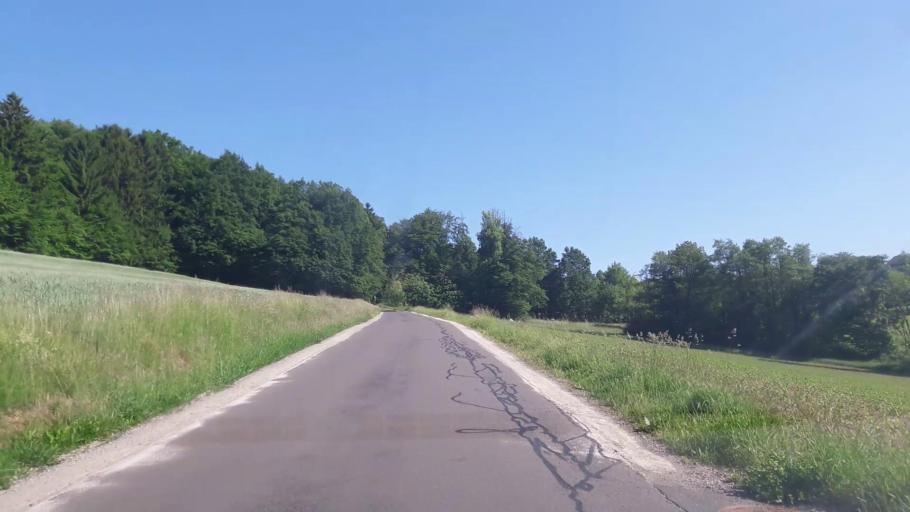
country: AT
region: Styria
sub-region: Politischer Bezirk Hartberg-Fuerstenfeld
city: UEbersbach
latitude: 46.9999
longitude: 16.0440
